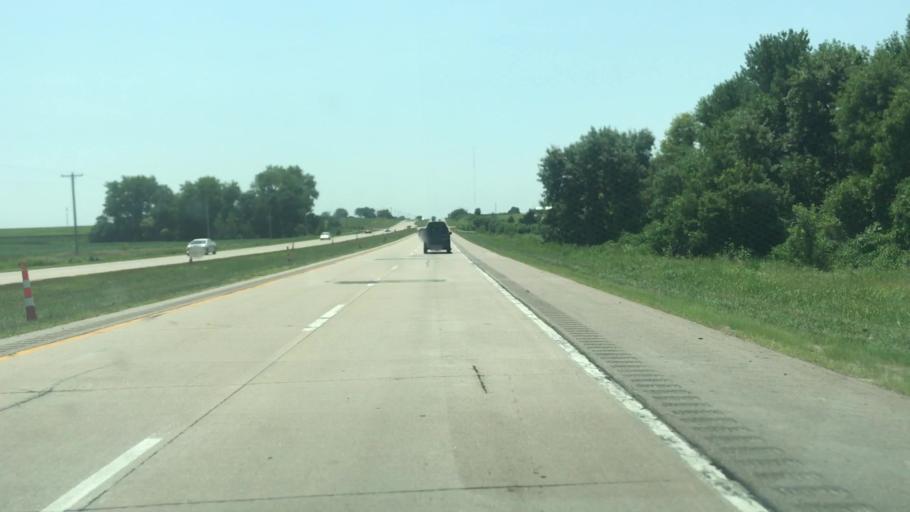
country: US
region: Nebraska
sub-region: Adams County
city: Hastings
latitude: 40.6737
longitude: -98.3823
